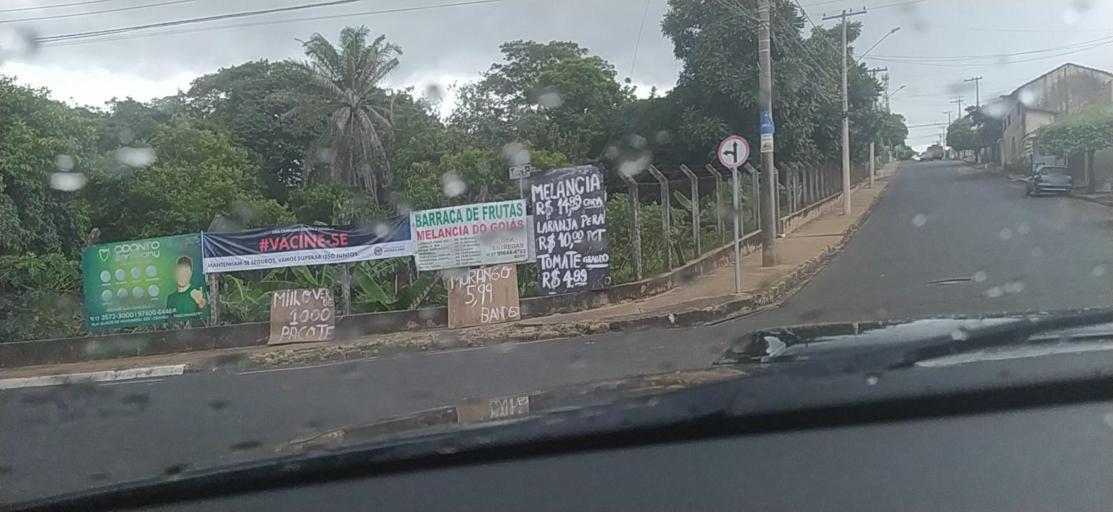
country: BR
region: Sao Paulo
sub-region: Pindorama
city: Pindorama
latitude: -21.1849
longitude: -48.9035
